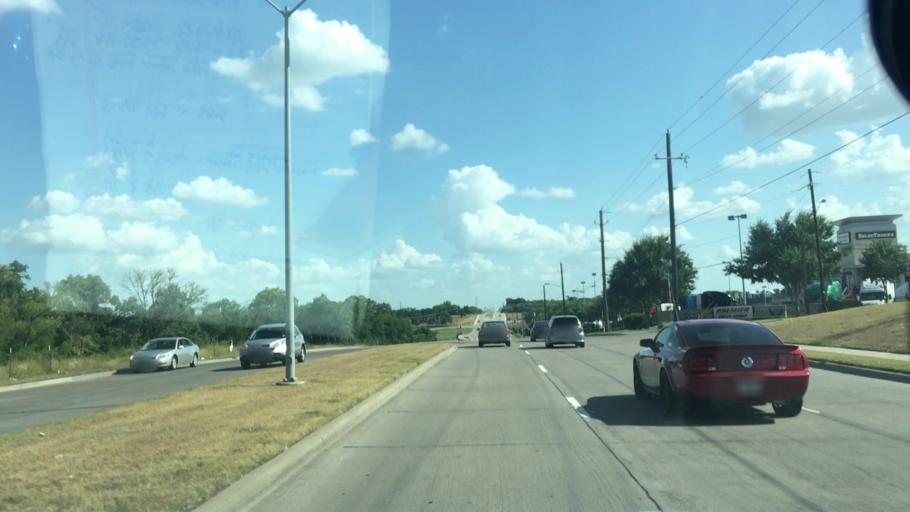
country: US
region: Texas
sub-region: Dallas County
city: Hutchins
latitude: 32.6523
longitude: -96.7508
